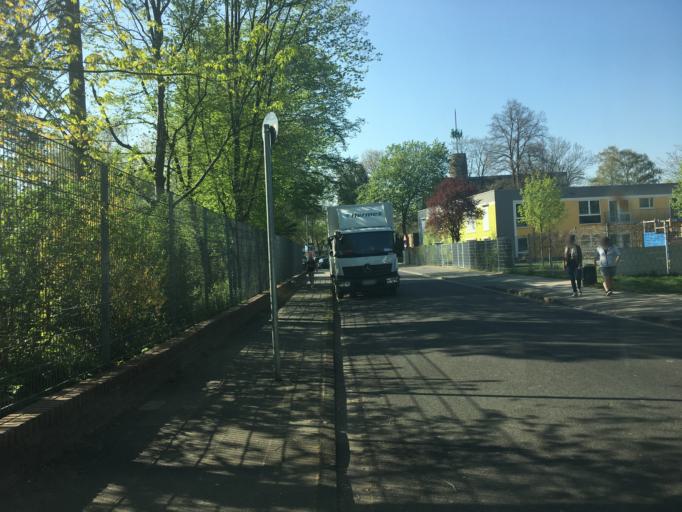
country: DE
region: North Rhine-Westphalia
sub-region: Regierungsbezirk Koln
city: Leverkusen
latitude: 50.9973
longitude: 6.9906
